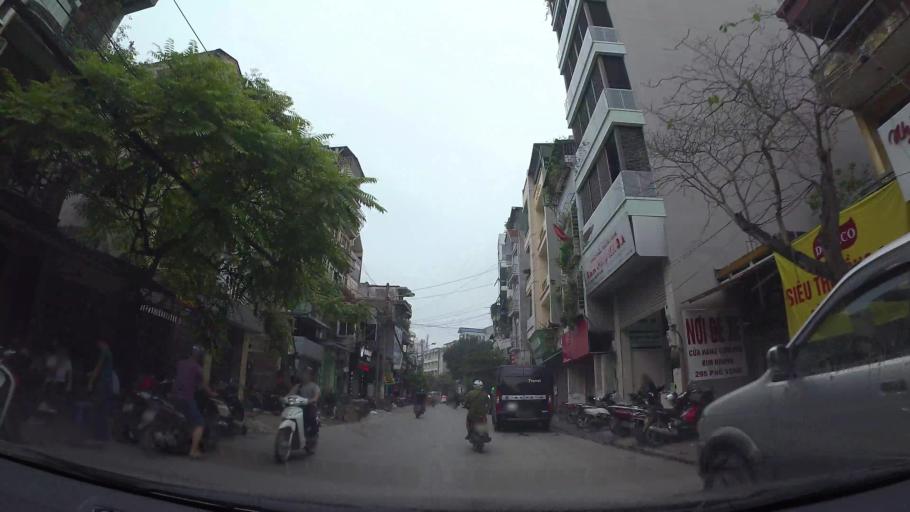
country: VN
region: Ha Noi
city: Hai BaTrung
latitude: 20.9943
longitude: 105.8423
